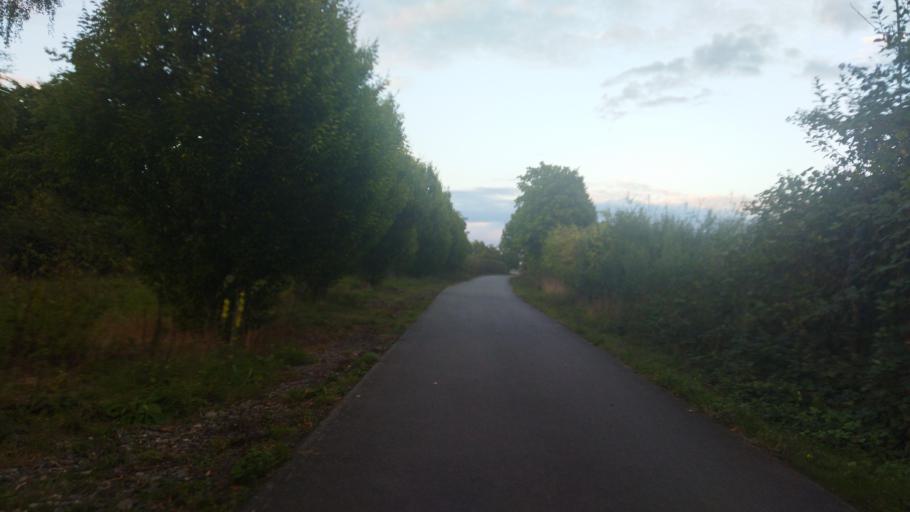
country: DE
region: North Rhine-Westphalia
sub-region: Regierungsbezirk Munster
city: Billerbeck
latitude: 52.0255
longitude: 7.2825
